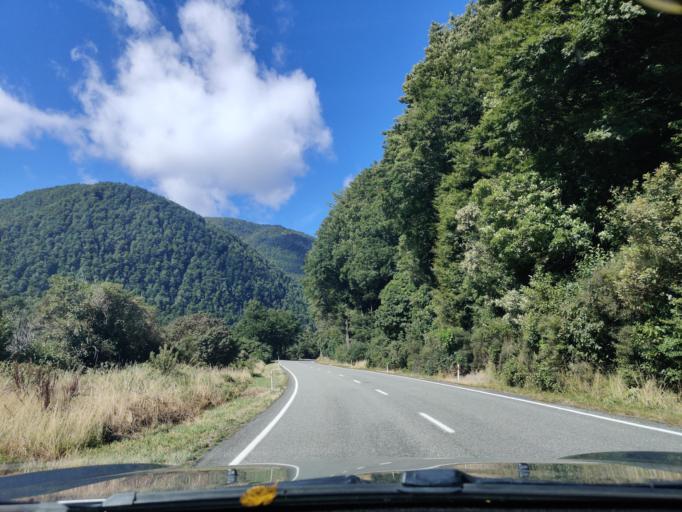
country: NZ
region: West Coast
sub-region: Buller District
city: Westport
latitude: -42.3559
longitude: 172.2469
